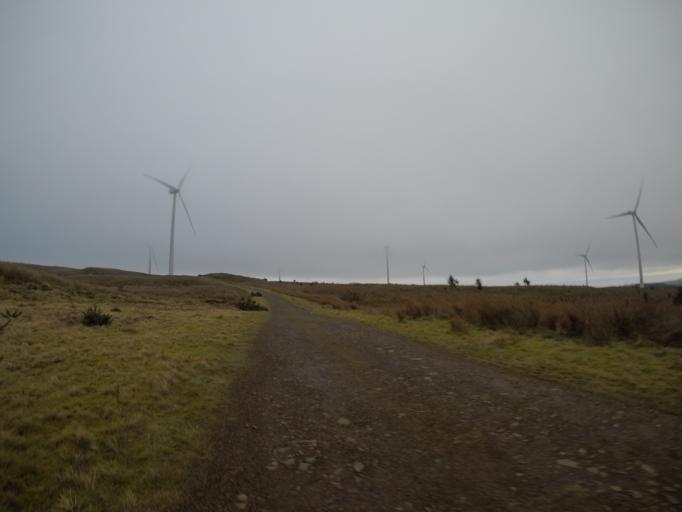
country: GB
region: Scotland
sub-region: North Ayrshire
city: Dalry
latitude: 55.7360
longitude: -4.7867
